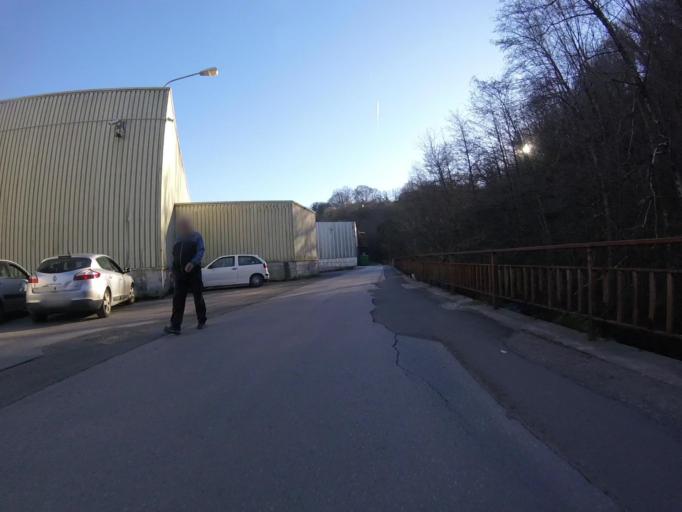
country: ES
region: Basque Country
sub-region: Provincia de Guipuzcoa
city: Errenteria
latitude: 43.3004
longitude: -1.8843
